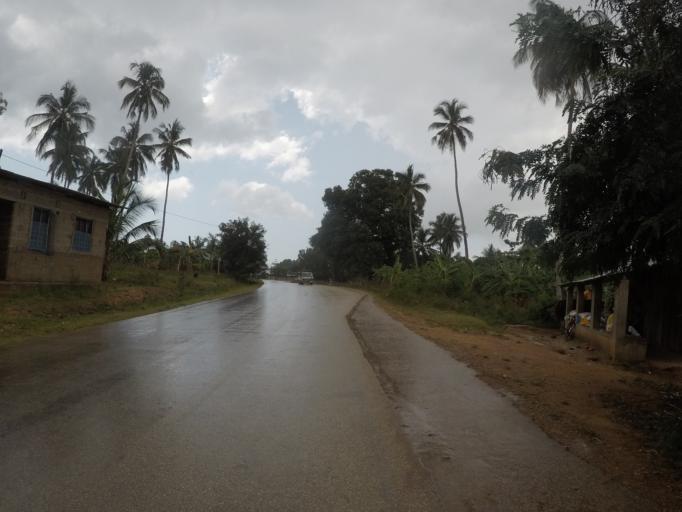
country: TZ
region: Zanzibar North
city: Mkokotoni
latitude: -5.9573
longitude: 39.1944
